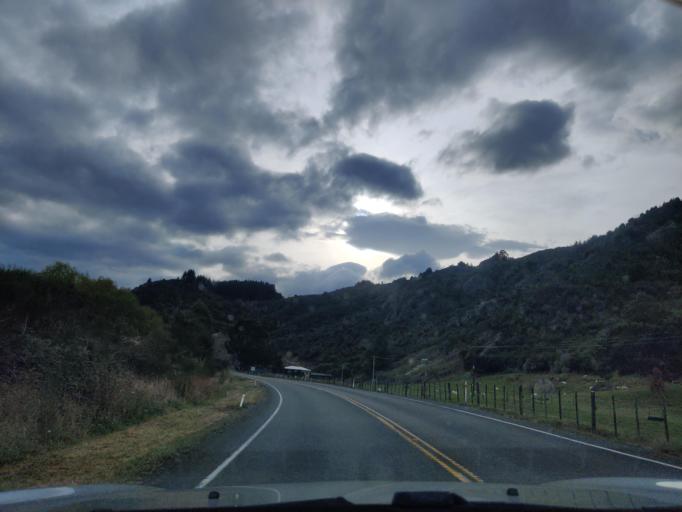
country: NZ
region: West Coast
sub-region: Buller District
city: Westport
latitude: -41.7968
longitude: 172.3612
